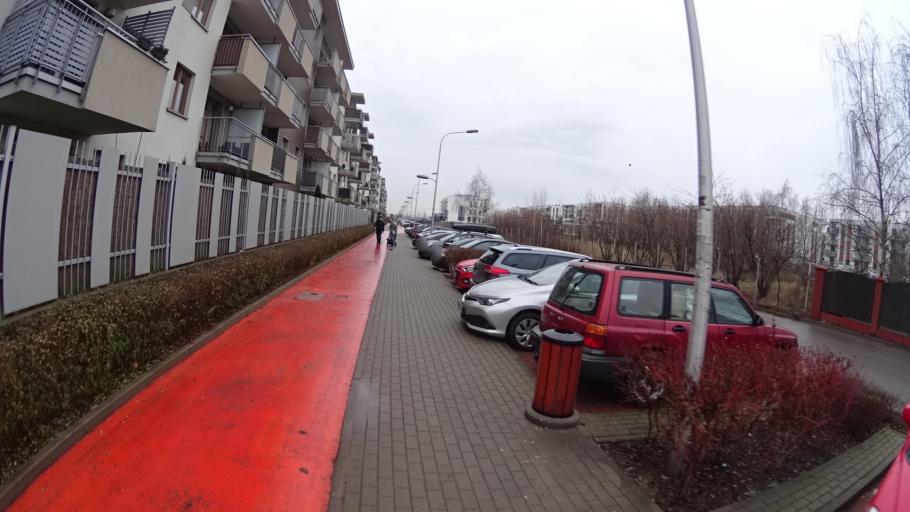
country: PL
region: Masovian Voivodeship
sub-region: Warszawa
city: Bemowo
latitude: 52.2311
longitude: 20.8914
